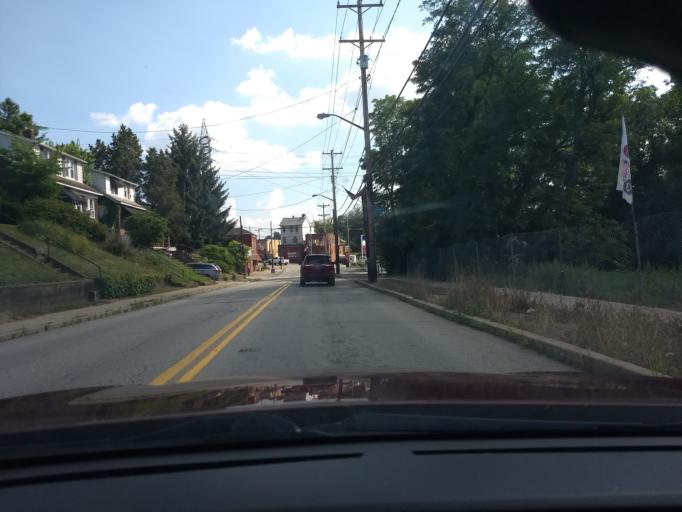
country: US
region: Pennsylvania
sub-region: Allegheny County
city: West Homestead
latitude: 40.3708
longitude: -79.9126
